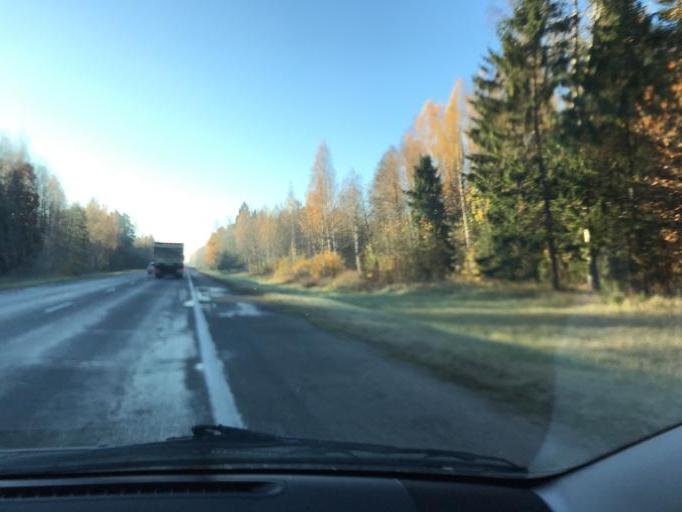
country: BY
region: Vitebsk
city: Vitebsk
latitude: 54.9486
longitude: 30.3616
